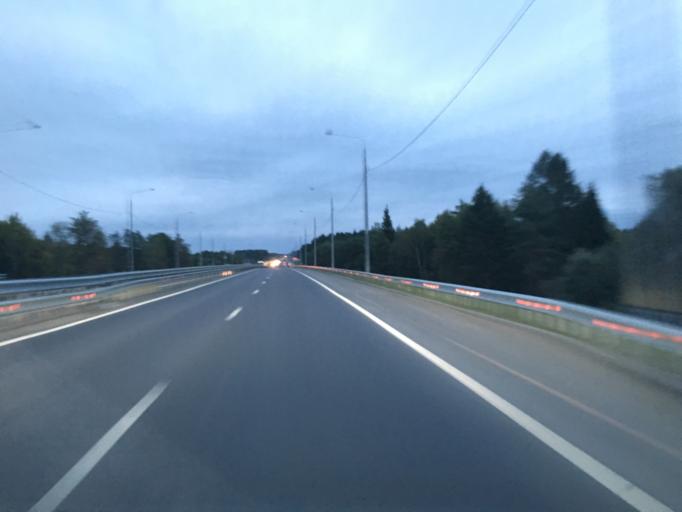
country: RU
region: Kaluga
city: Maloyaroslavets
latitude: 54.9138
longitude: 36.3881
